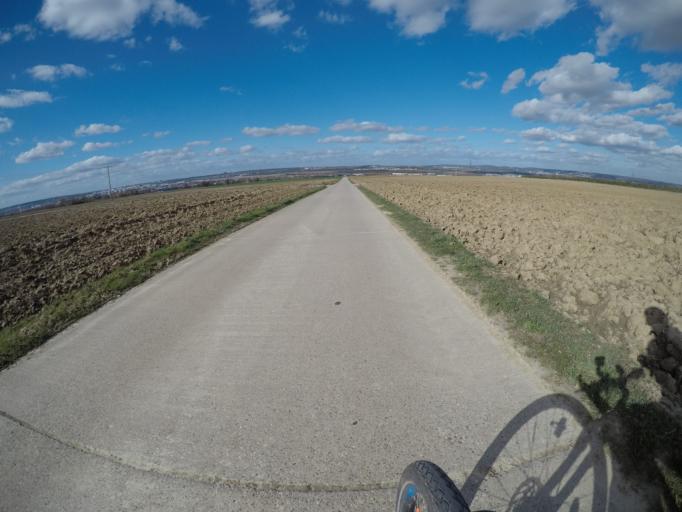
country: DE
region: Baden-Wuerttemberg
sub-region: Regierungsbezirk Stuttgart
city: Filderstadt
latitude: 48.6594
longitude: 9.2488
